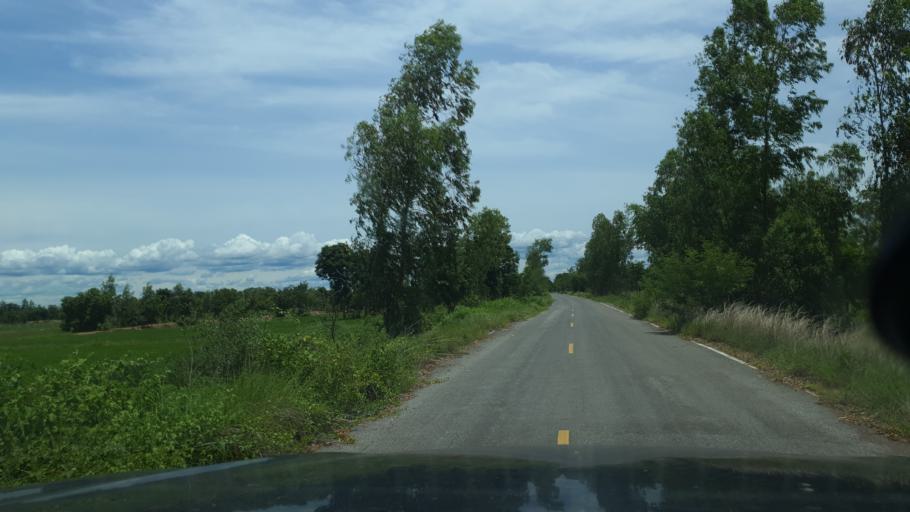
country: TH
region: Sukhothai
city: Ban Na
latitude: 17.1020
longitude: 99.6791
